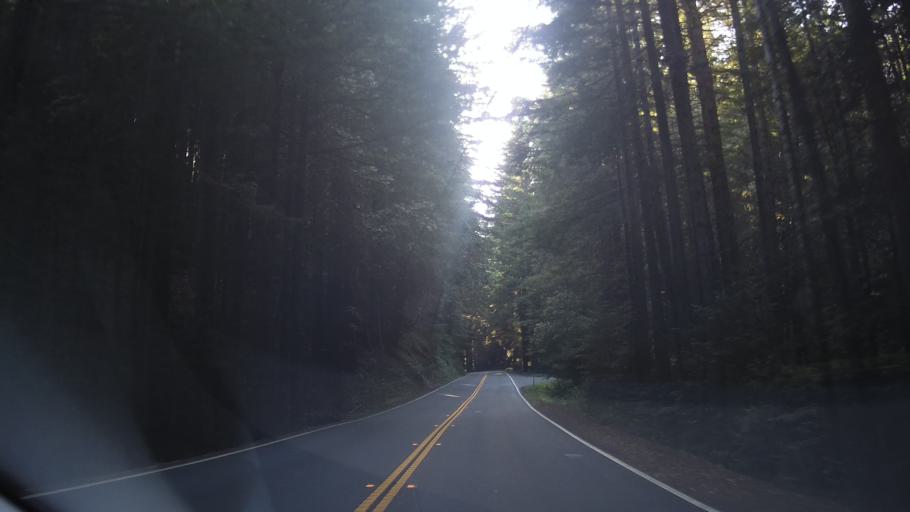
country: US
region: California
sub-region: Mendocino County
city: Brooktrails
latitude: 39.3471
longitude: -123.5670
